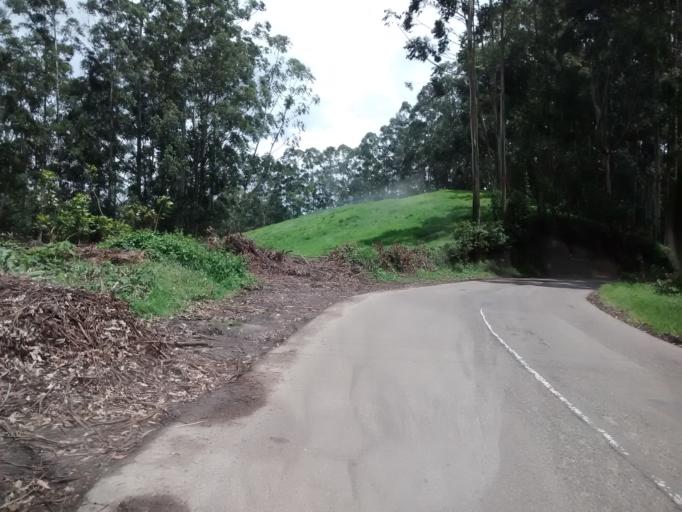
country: IN
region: Kerala
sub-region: Idukki
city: Munnar
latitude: 10.1096
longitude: 77.1345
